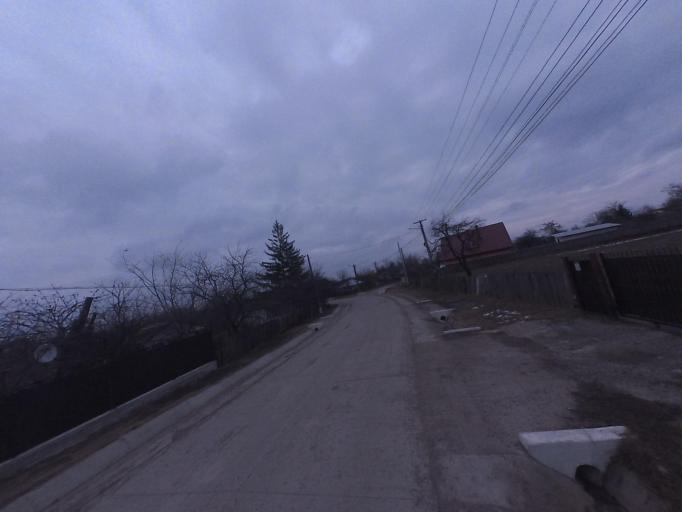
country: RO
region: Iasi
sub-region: Comuna Popricani
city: Popricani
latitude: 47.2904
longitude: 27.5066
